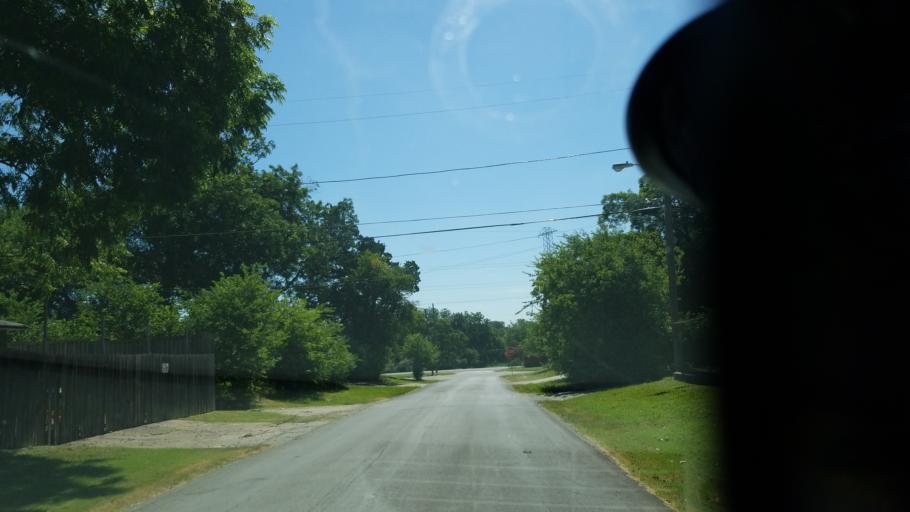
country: US
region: Texas
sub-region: Dallas County
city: Dallas
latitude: 32.7114
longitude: -96.8118
